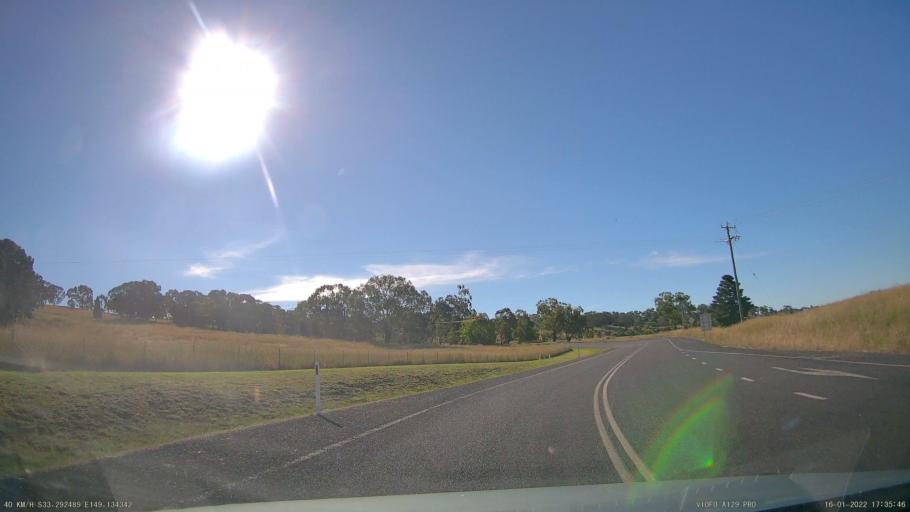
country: AU
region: New South Wales
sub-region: Orange Municipality
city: Orange
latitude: -33.2925
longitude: 149.1343
